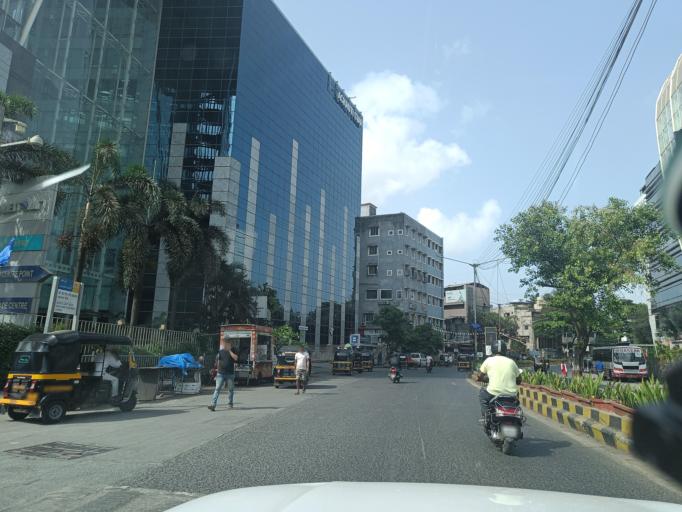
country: IN
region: Maharashtra
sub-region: Mumbai Suburban
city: Powai
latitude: 19.1190
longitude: 72.8703
